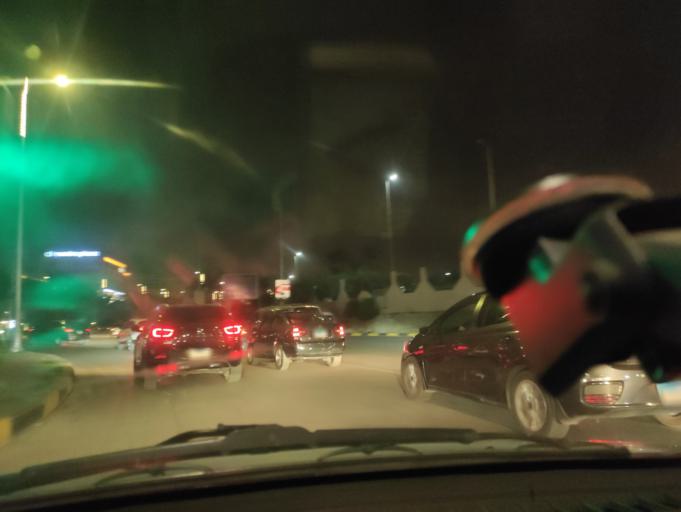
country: EG
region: Al Jizah
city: Awsim
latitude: 30.0226
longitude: 31.0045
